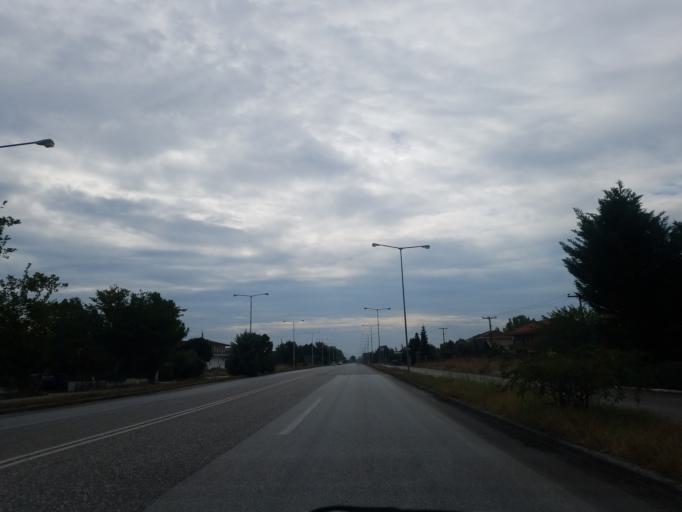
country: GR
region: Thessaly
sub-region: Trikala
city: Pyrgetos
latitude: 39.5826
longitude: 21.7405
